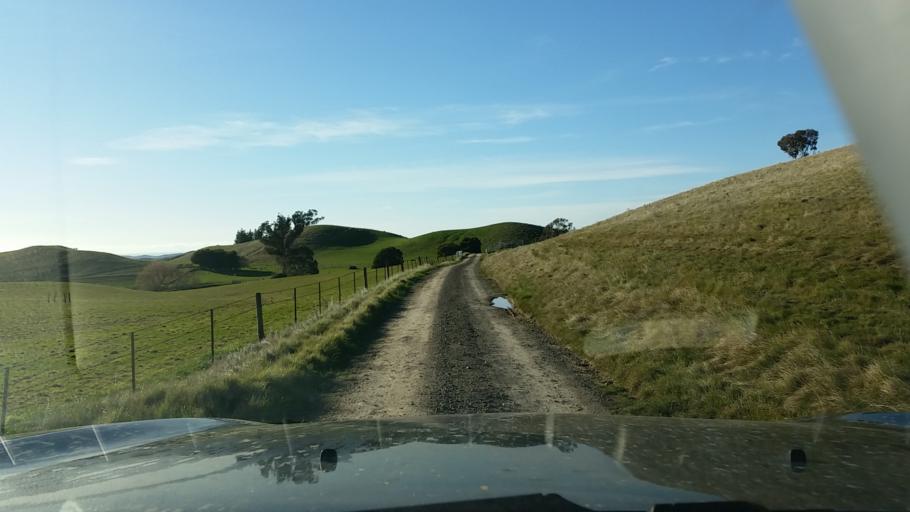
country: NZ
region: Marlborough
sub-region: Marlborough District
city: Blenheim
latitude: -41.7334
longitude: 174.0065
